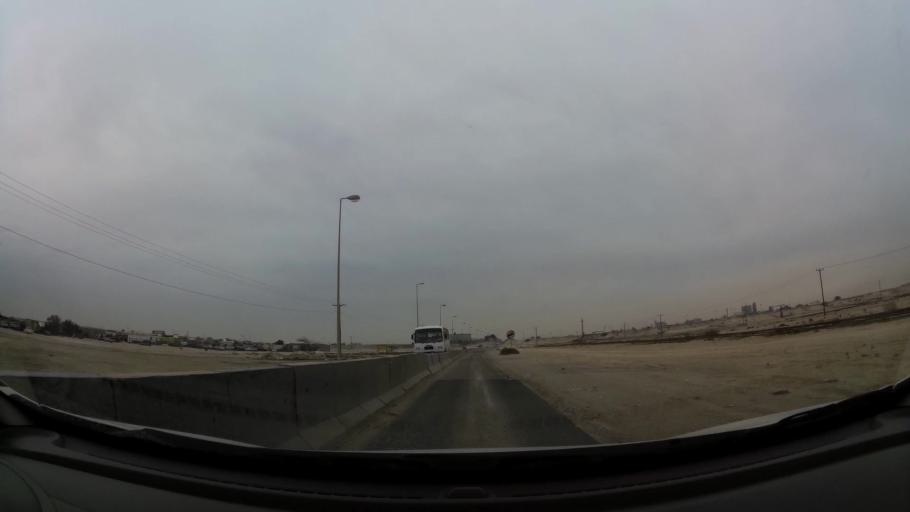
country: BH
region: Northern
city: Ar Rifa'
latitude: 26.0898
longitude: 50.5795
